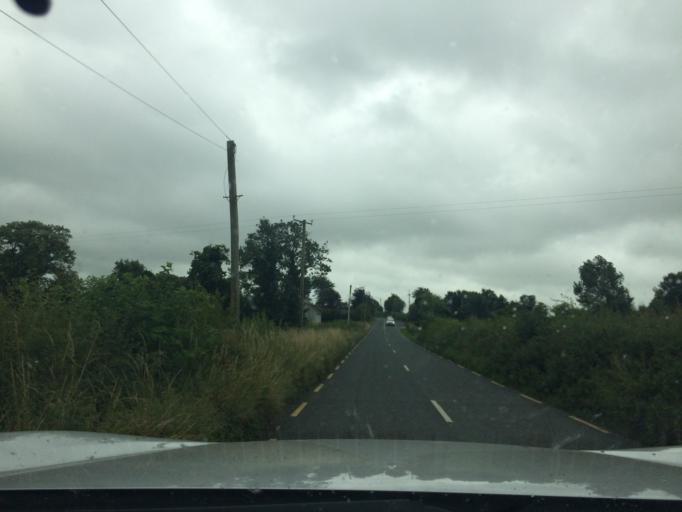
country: IE
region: Munster
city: Cashel
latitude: 52.5431
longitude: -7.8935
